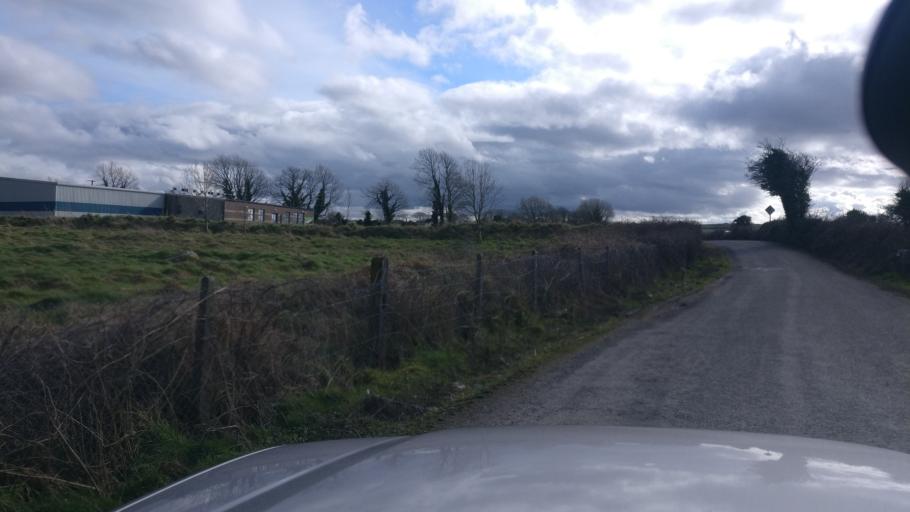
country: IE
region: Connaught
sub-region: County Galway
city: Loughrea
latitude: 53.1966
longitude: -8.5402
